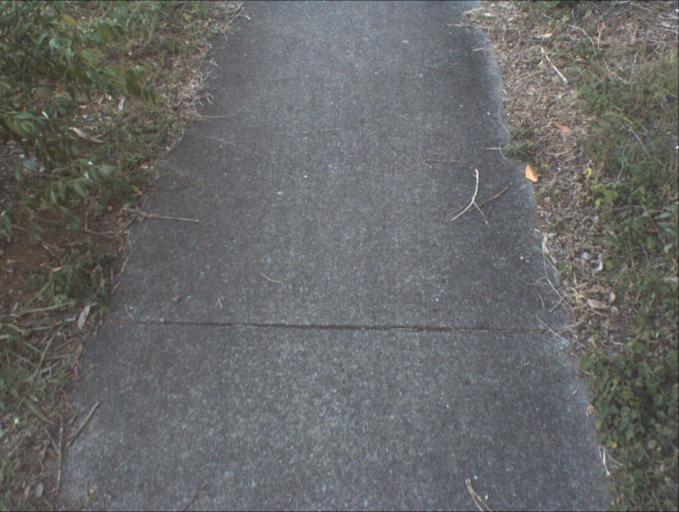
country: AU
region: Queensland
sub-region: Logan
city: Beenleigh
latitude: -27.6747
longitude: 153.2051
